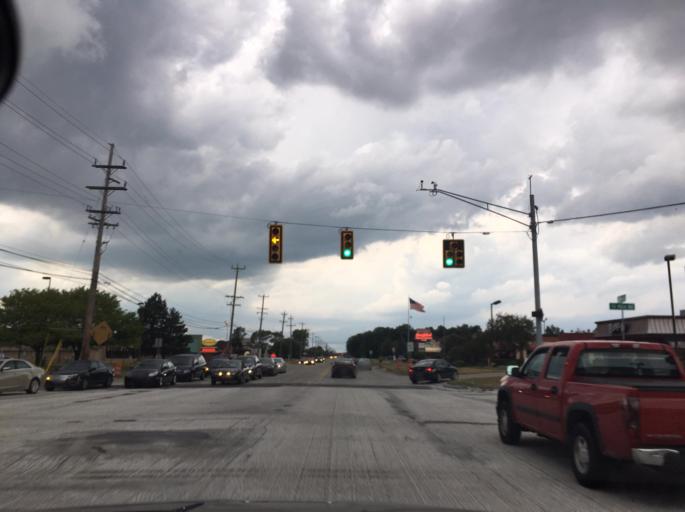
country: US
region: Michigan
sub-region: Macomb County
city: Clinton
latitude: 42.6129
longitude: -82.9529
